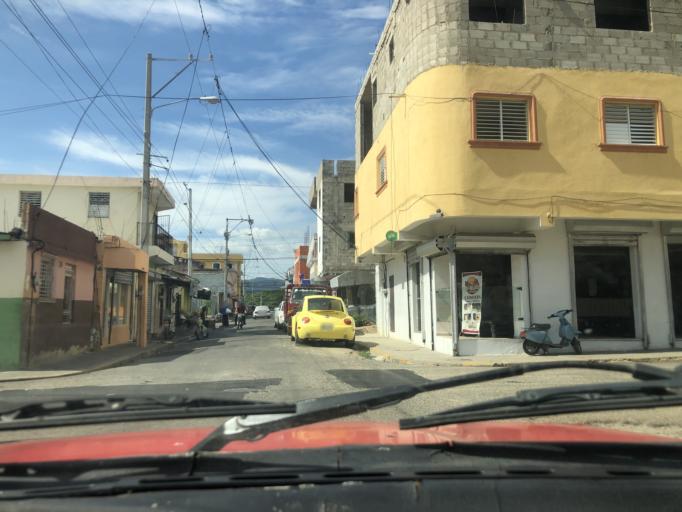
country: DO
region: Santiago
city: Santiago de los Caballeros
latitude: 19.4613
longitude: -70.7080
